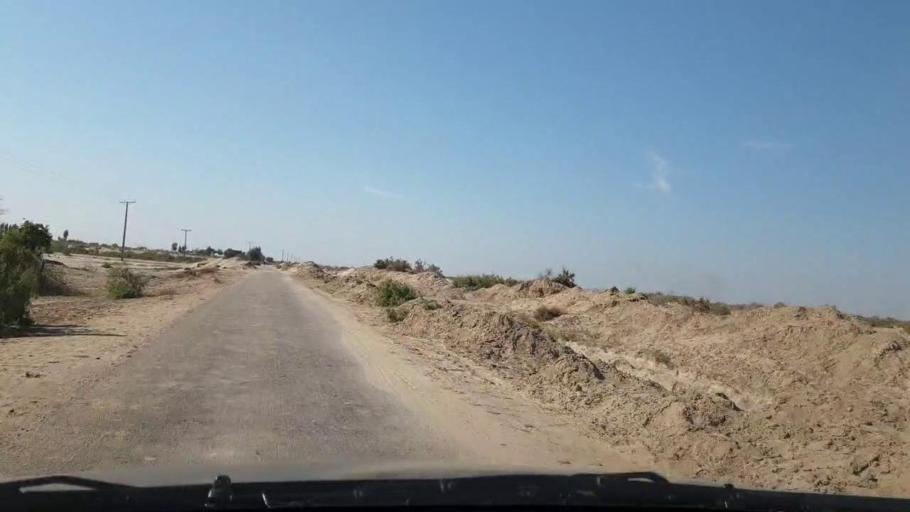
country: PK
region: Sindh
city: Khadro
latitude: 26.2703
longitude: 68.7884
